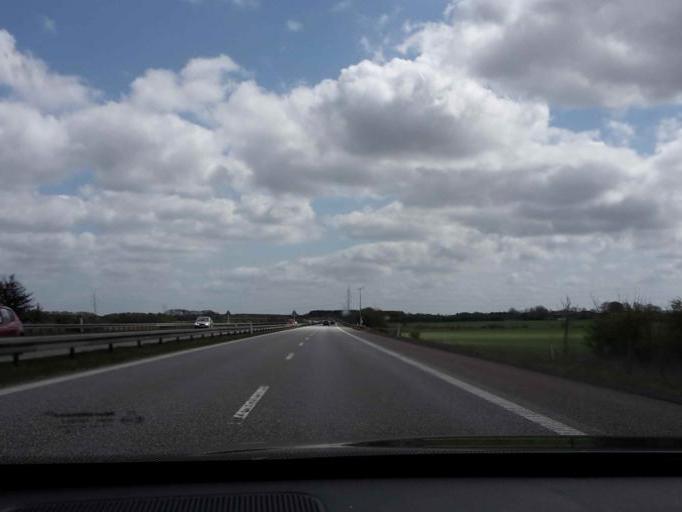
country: DK
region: South Denmark
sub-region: Esbjerg Kommune
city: Tjaereborg
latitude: 55.5153
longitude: 8.6262
